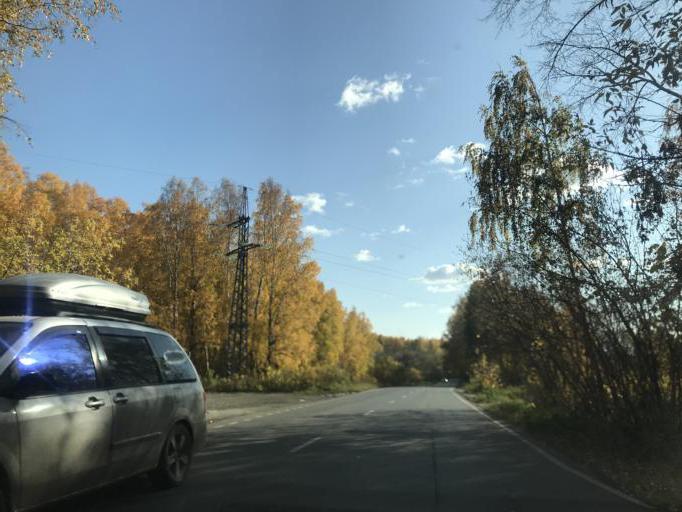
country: RU
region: Chelyabinsk
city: Dolgoderevenskoye
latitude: 55.2657
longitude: 61.3647
